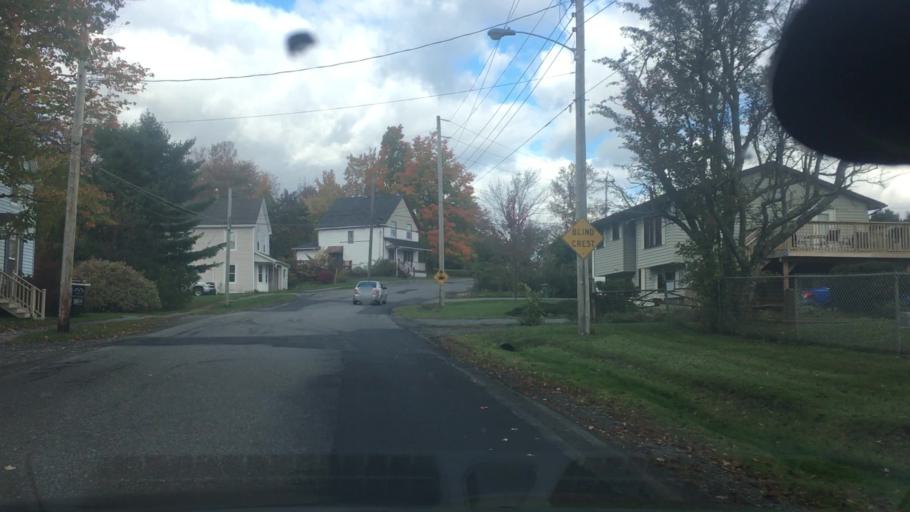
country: CA
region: Nova Scotia
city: Windsor
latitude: 44.9864
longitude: -64.1345
